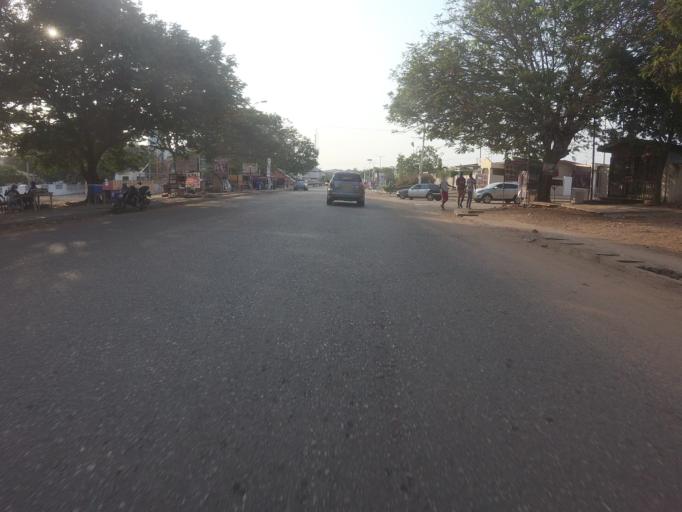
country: GH
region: Greater Accra
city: Nungua
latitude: 5.6232
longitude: -0.0602
